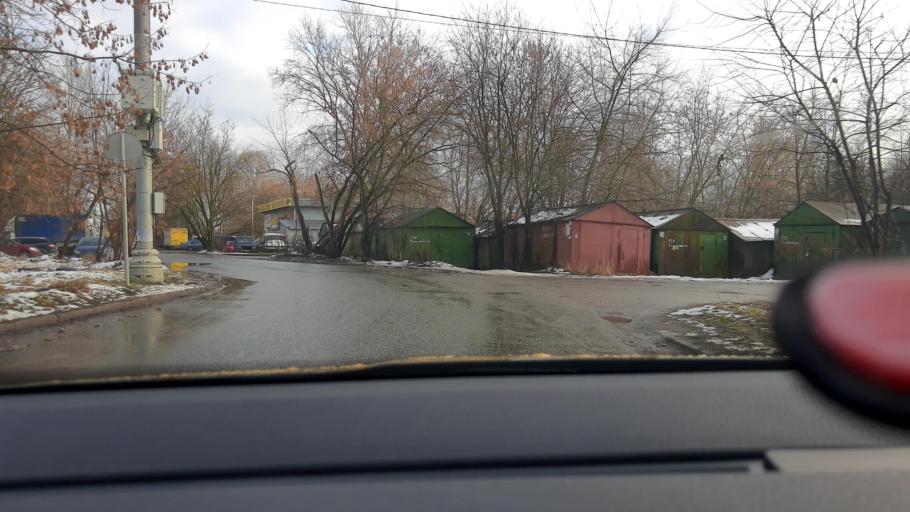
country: RU
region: Moskovskaya
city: Pushkino
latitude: 55.9924
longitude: 37.8618
